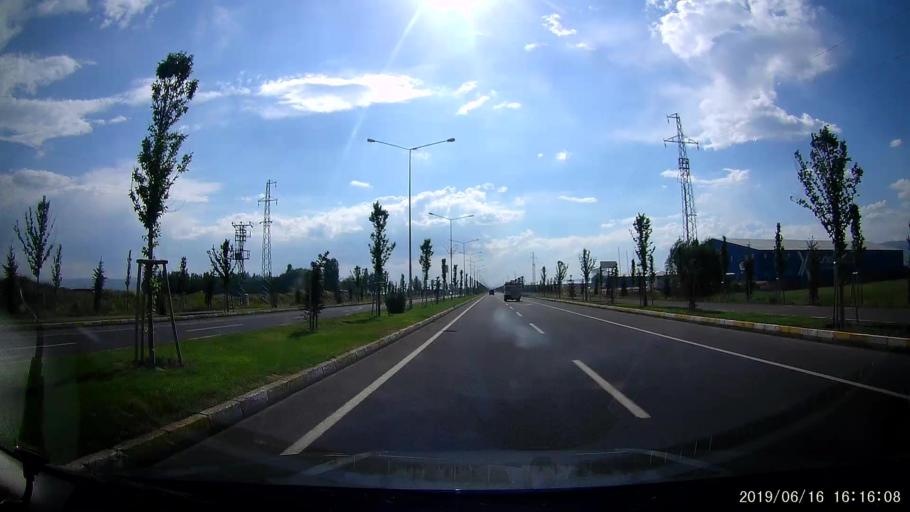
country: TR
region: Erzurum
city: Erzurum
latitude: 39.9626
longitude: 41.2129
